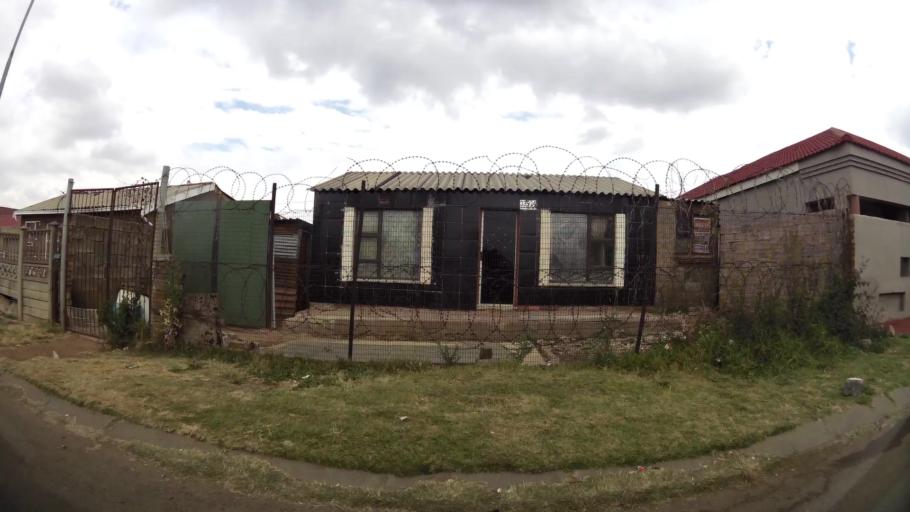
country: ZA
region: Gauteng
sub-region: City of Johannesburg Metropolitan Municipality
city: Soweto
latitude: -26.2693
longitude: 27.8739
